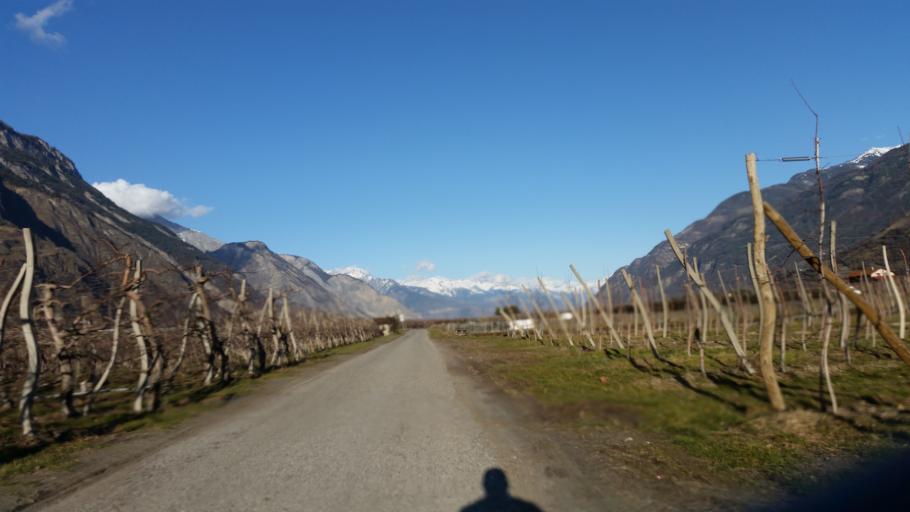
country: CH
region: Valais
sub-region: Martigny District
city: Charrat-les-Chenes
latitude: 46.1382
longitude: 7.1399
